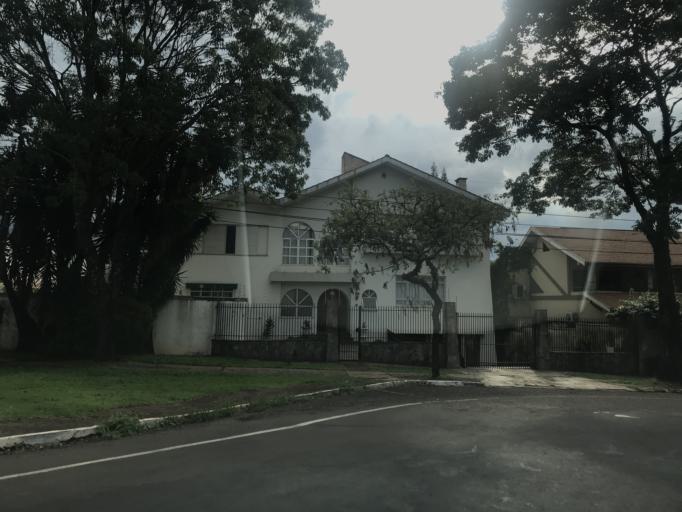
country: BR
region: Parana
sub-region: Maringa
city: Maringa
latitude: -23.4289
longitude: -51.9611
